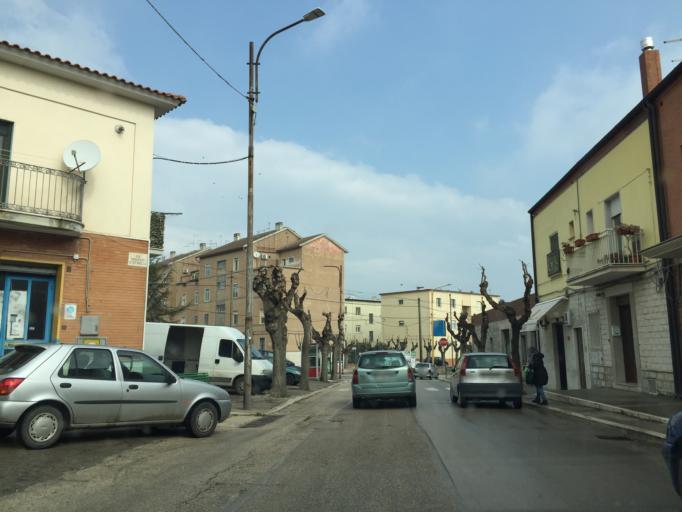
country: IT
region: Apulia
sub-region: Provincia di Foggia
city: Troia
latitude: 41.3631
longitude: 15.3133
